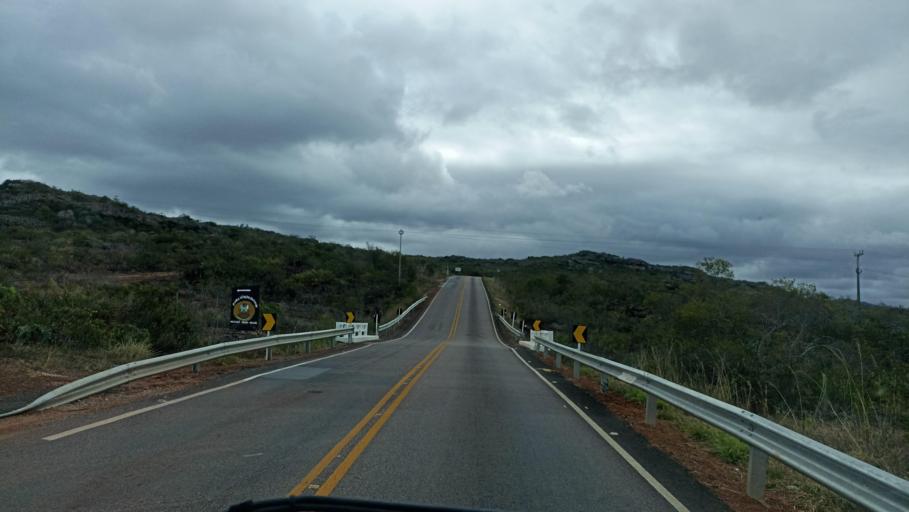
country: BR
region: Bahia
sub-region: Andarai
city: Vera Cruz
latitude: -12.9932
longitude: -41.3529
